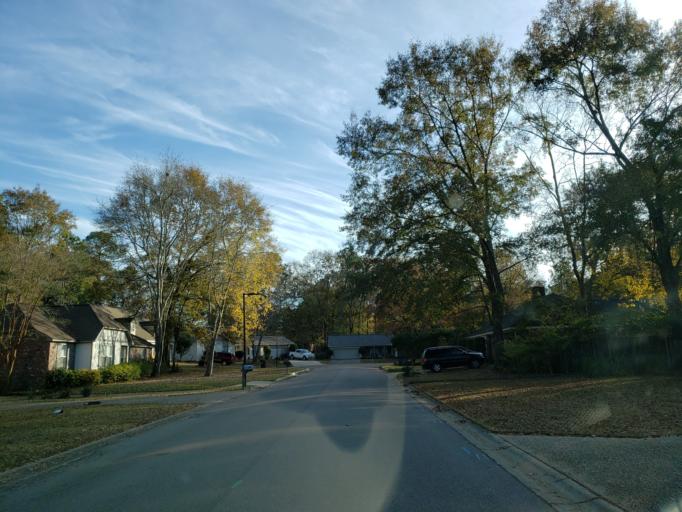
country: US
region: Mississippi
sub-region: Lamar County
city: West Hattiesburg
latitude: 31.2989
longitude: -89.3359
